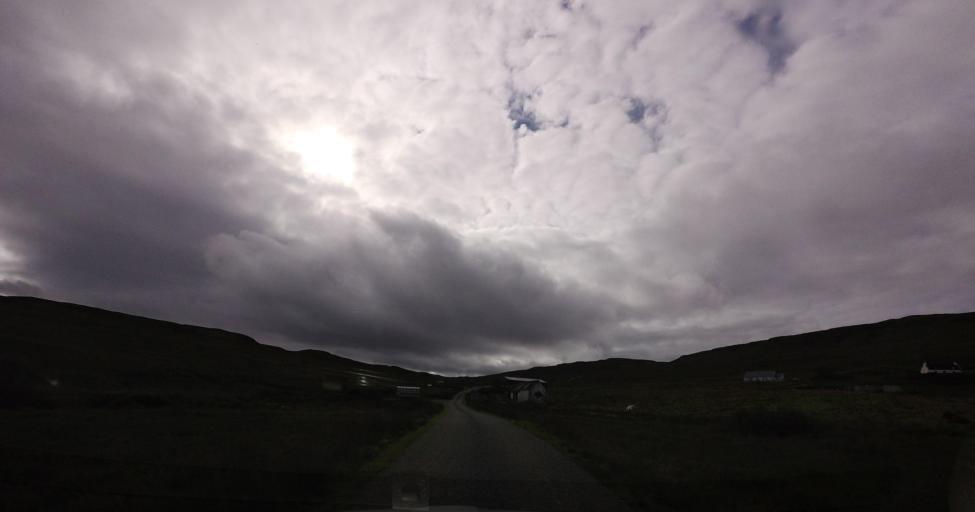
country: GB
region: Scotland
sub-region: Highland
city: Isle of Skye
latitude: 57.4198
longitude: -6.2578
